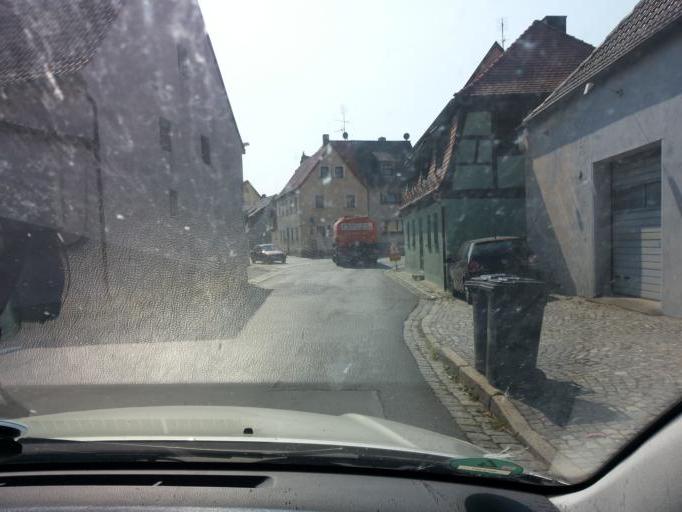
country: DE
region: Bavaria
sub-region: Regierungsbezirk Mittelfranken
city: Markt Erlbach
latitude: 49.4928
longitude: 10.6492
